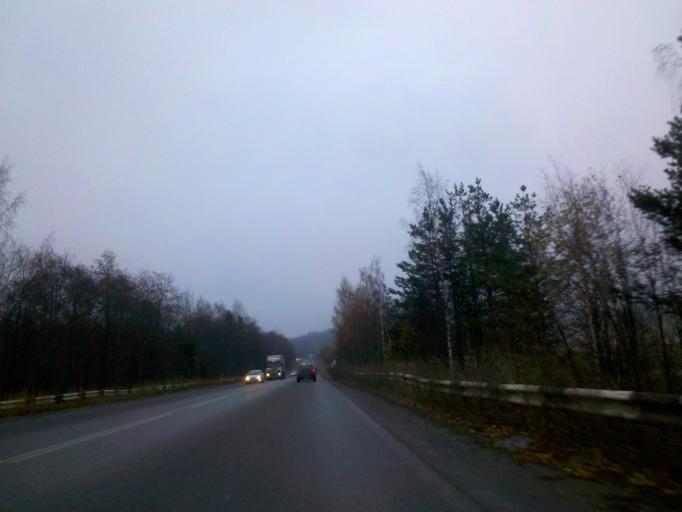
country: RU
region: Republic of Karelia
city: Petrozavodsk
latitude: 61.8228
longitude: 34.2295
